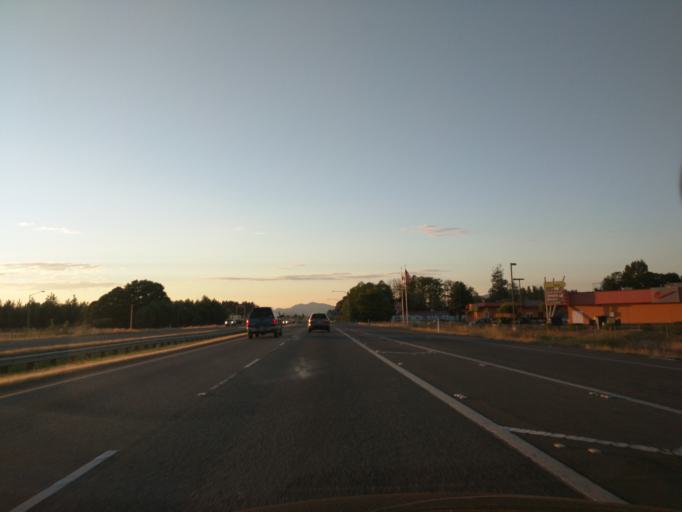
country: US
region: Washington
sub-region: Skagit County
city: Burlington
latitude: 48.4556
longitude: -122.3413
